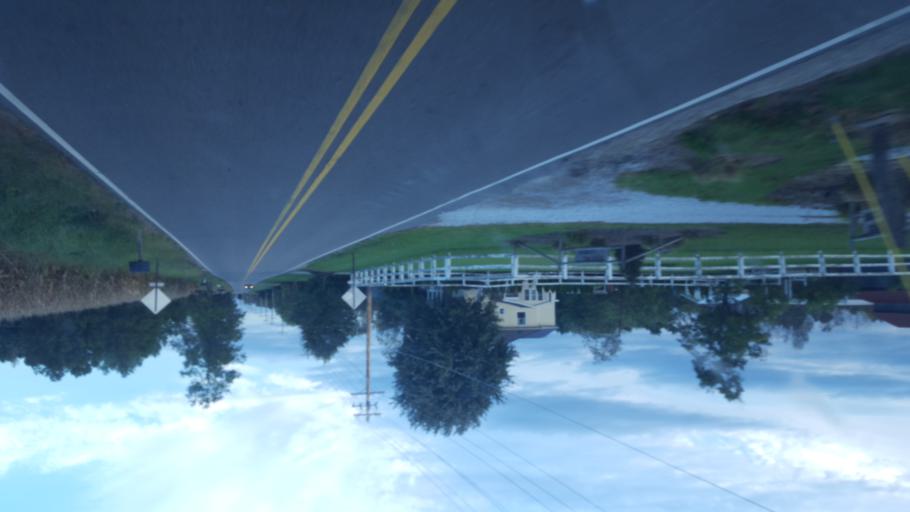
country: US
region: Ohio
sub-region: Franklin County
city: New Albany
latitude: 40.0990
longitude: -82.7538
